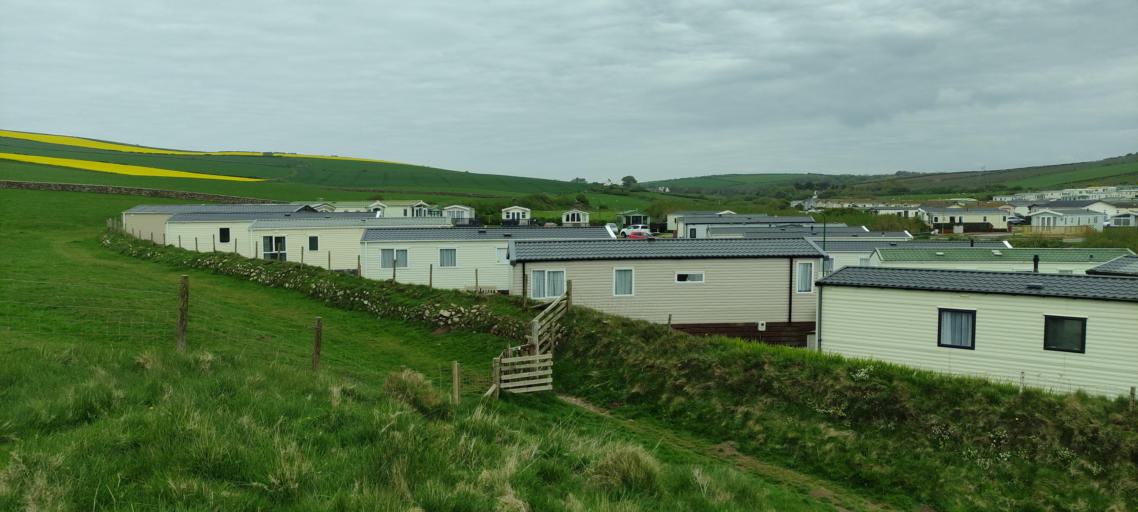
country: GB
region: England
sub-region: Cumbria
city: Saint Bees
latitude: 54.4916
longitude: -3.6085
